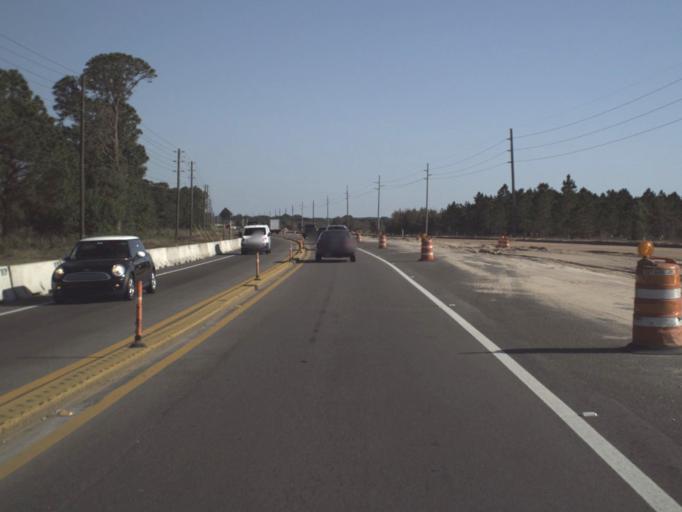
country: US
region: Florida
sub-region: Lake County
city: Clermont
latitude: 28.4747
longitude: -81.7155
